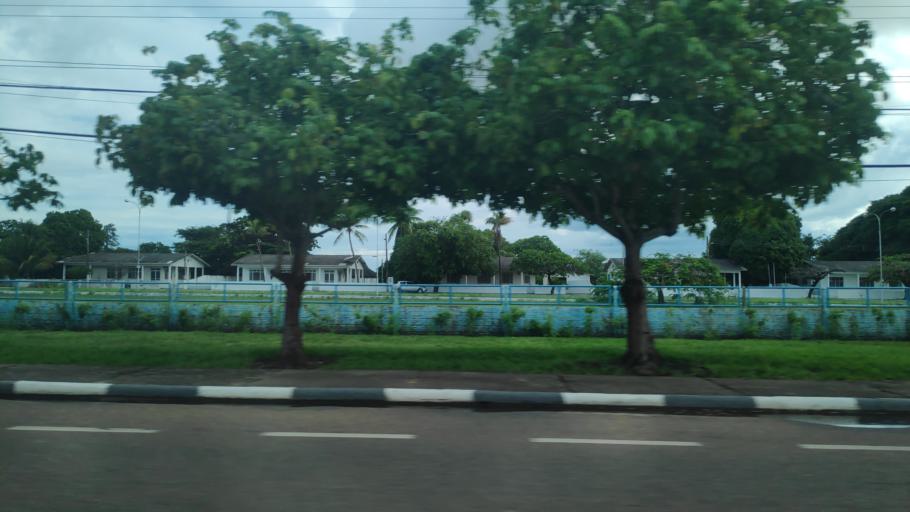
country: BR
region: Roraima
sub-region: Boa Vista
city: Boa Vista
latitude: 2.8305
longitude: -60.6839
